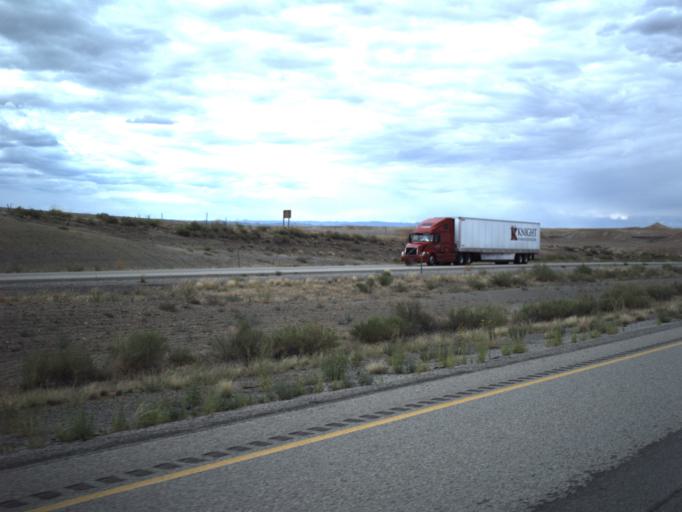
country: US
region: Utah
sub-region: Grand County
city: Moab
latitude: 38.9387
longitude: -109.4068
